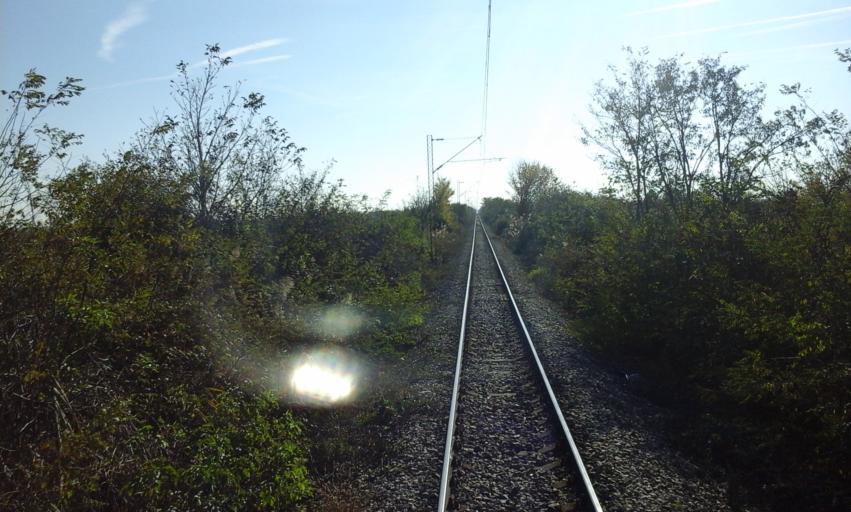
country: RS
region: Autonomna Pokrajina Vojvodina
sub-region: Severnobacki Okrug
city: Subotica
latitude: 46.0536
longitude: 19.6859
